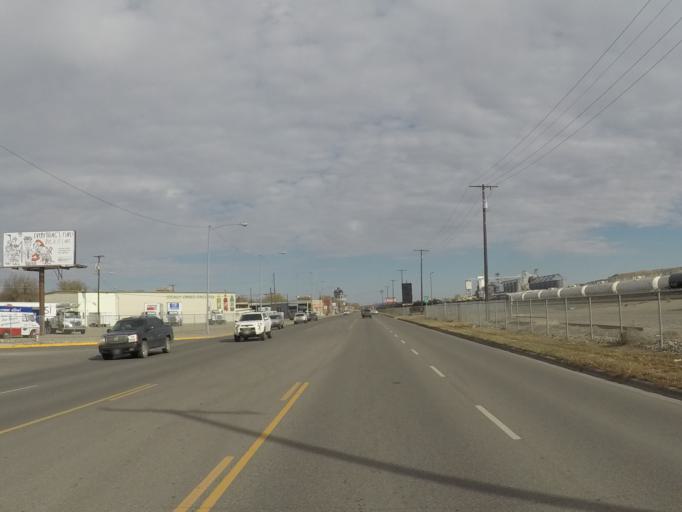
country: US
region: Montana
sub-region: Yellowstone County
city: Billings
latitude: 45.7718
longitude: -108.5243
